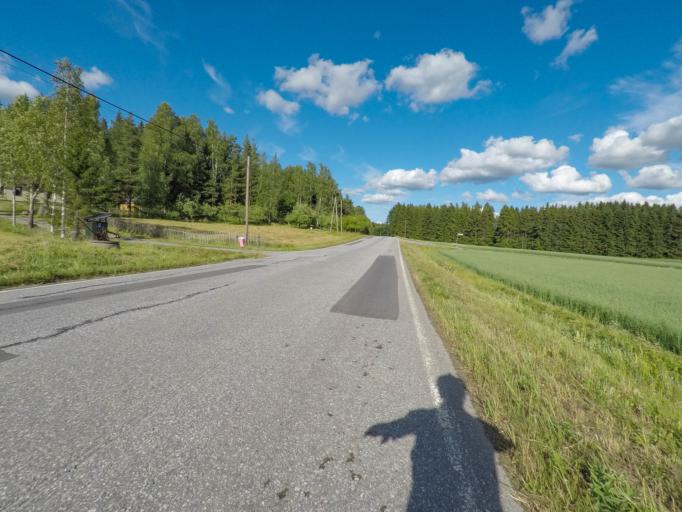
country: FI
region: South Karelia
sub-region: Imatra
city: Imatra
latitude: 61.1297
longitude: 28.7190
